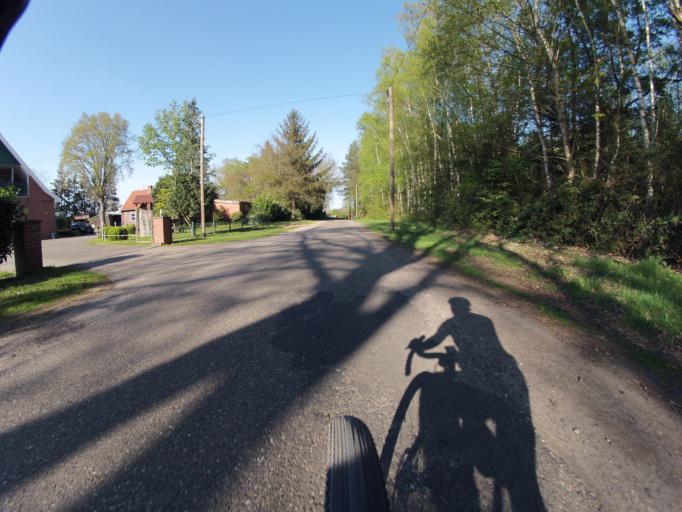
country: DE
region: Lower Saxony
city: Schuttorf
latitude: 52.3401
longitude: 7.2212
